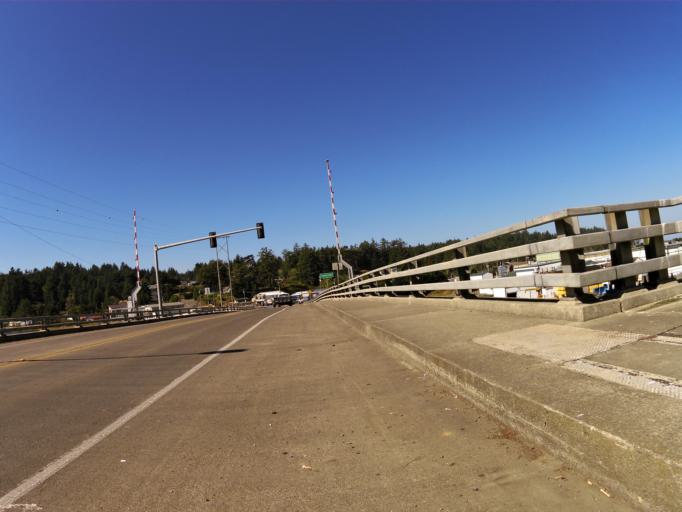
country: US
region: Oregon
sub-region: Coos County
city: Barview
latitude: 43.3390
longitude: -124.3214
